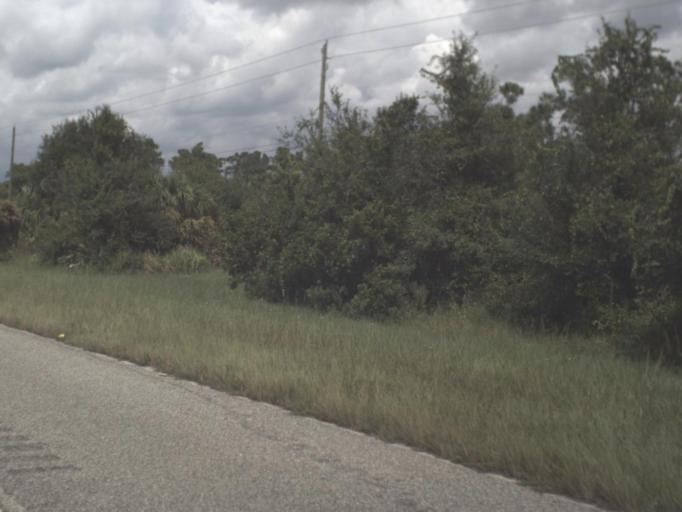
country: US
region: Florida
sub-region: Charlotte County
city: Harbour Heights
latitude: 26.9966
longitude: -82.0333
